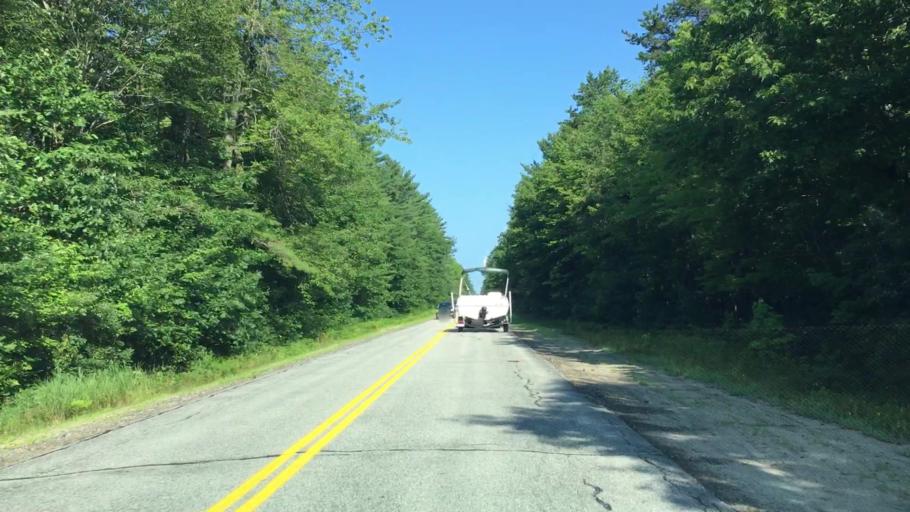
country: US
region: Maine
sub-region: Androscoggin County
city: Poland
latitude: 44.0455
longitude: -70.3594
